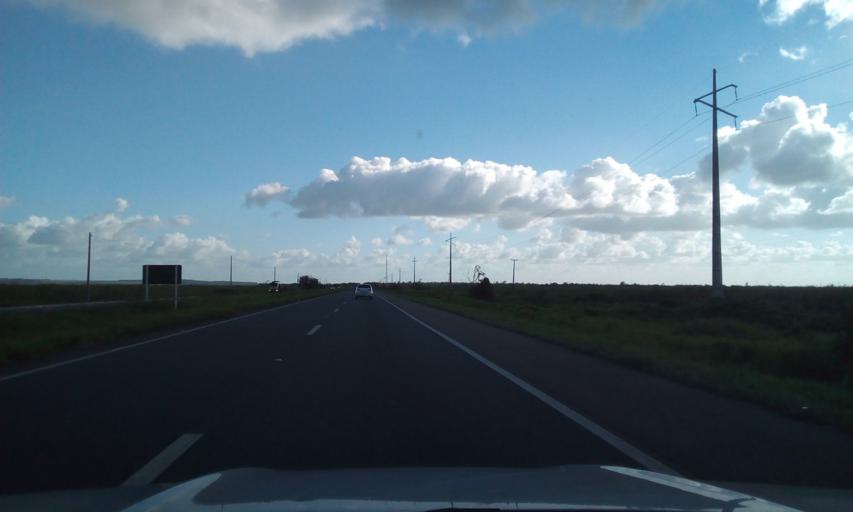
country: BR
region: Paraiba
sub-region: Cruz Do Espirito Santo
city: Cruz do Espirito Santo
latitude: -7.1898
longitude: -35.0618
